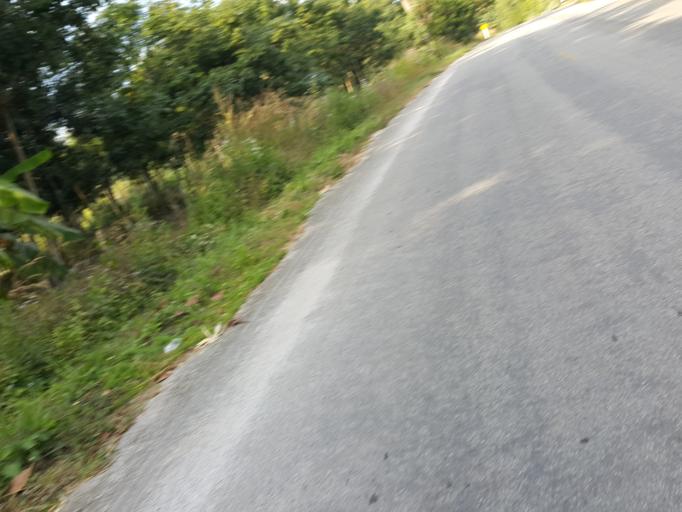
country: TH
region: Lamphun
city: Thung Hua Chang
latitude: 18.1073
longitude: 99.0161
